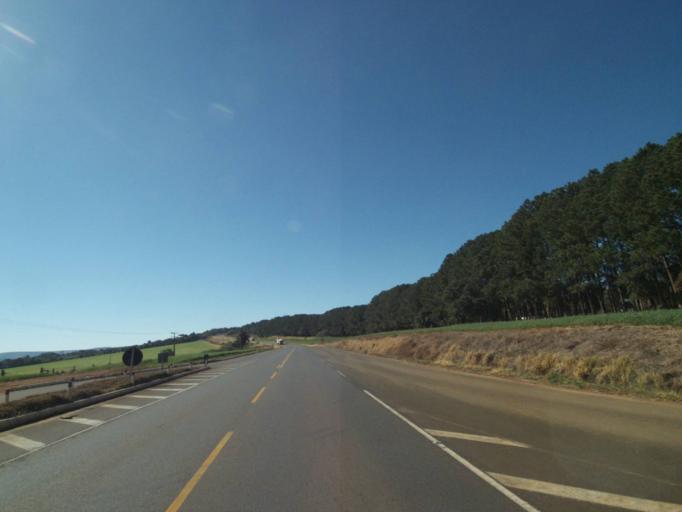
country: BR
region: Parana
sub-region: Tibagi
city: Tibagi
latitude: -24.4172
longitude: -50.3682
